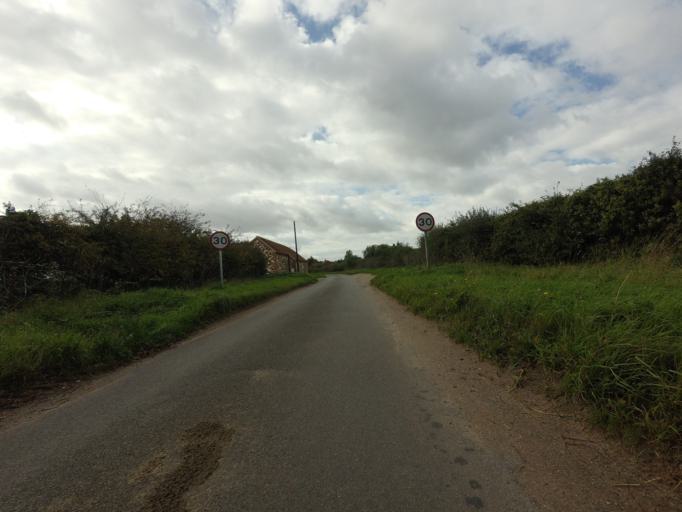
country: GB
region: England
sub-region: Norfolk
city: Hunstanton
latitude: 52.9335
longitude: 0.5461
